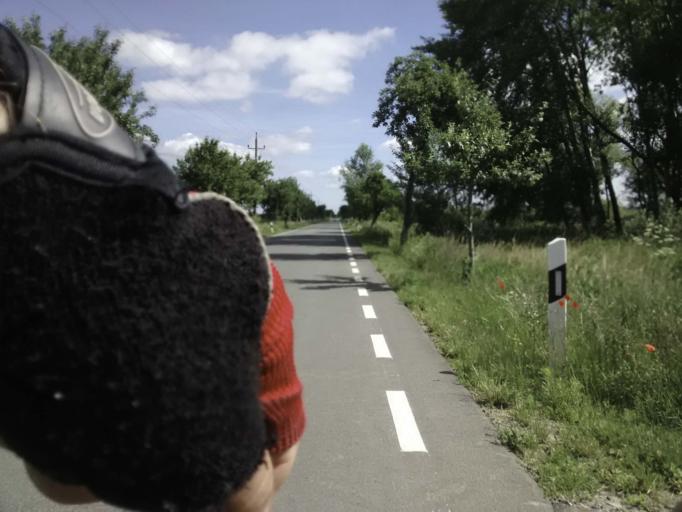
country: DE
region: Saxony-Anhalt
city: Jerichow
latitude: 52.4607
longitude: 11.9758
